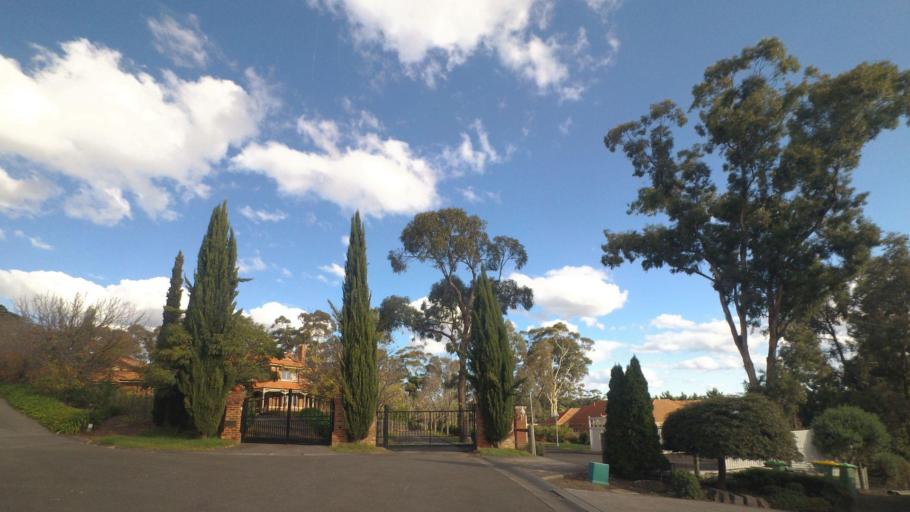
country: AU
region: Victoria
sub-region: Banyule
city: Lower Plenty
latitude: -37.7378
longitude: 145.1213
